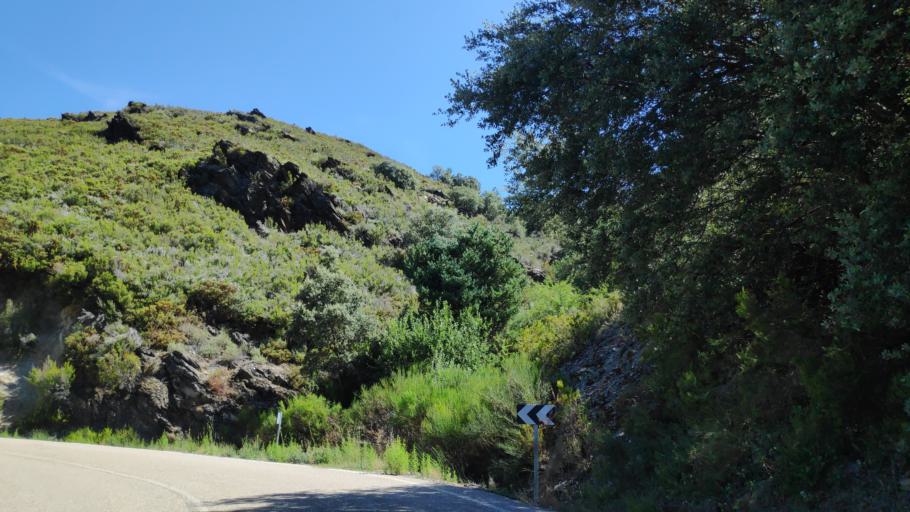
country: ES
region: Castille and Leon
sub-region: Provincia de Zamora
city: Requejo
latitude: 41.9890
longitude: -6.7042
